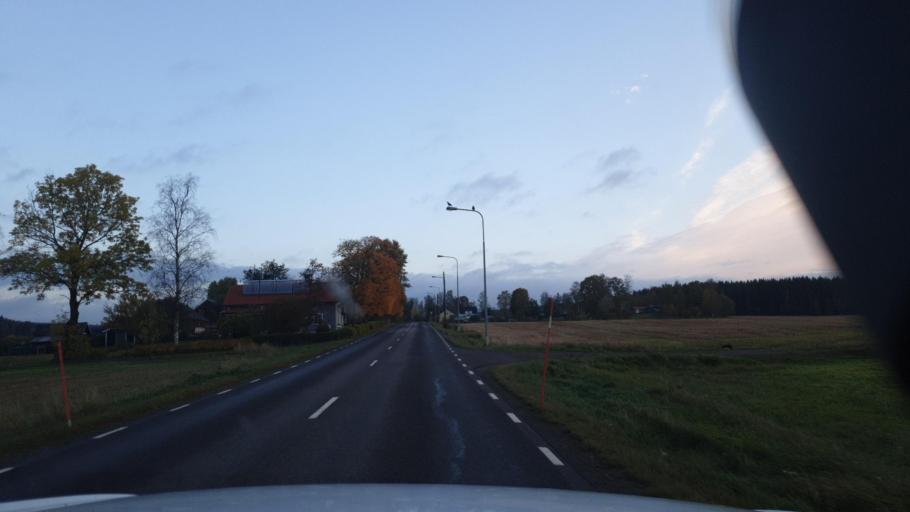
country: SE
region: Vaermland
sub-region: Arvika Kommun
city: Arvika
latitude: 59.7626
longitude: 12.5460
